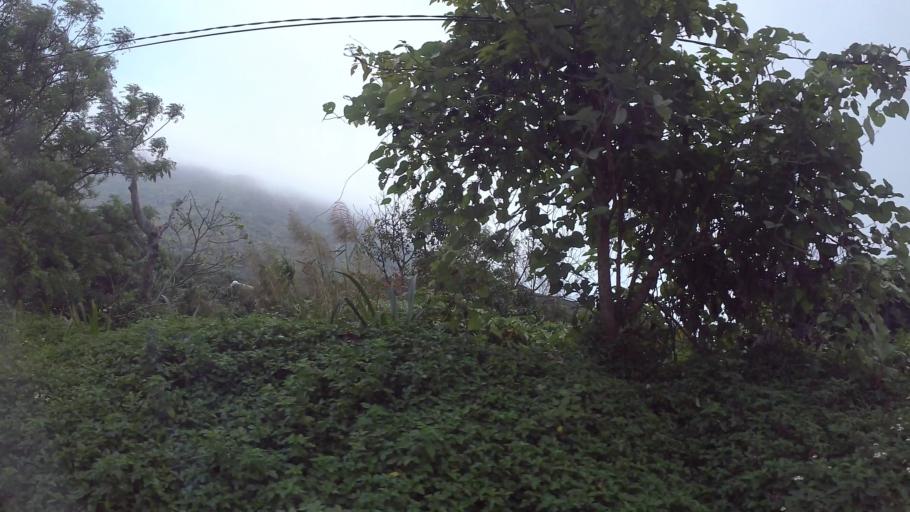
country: VN
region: Da Nang
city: Son Tra
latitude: 16.1163
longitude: 108.3081
